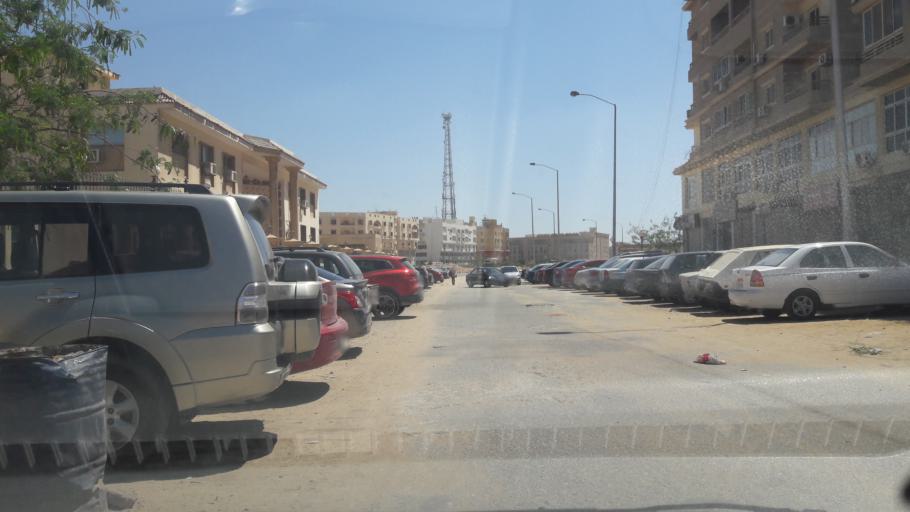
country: EG
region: Al Jizah
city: Madinat Sittah Uktubar
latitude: 29.9659
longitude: 30.9318
